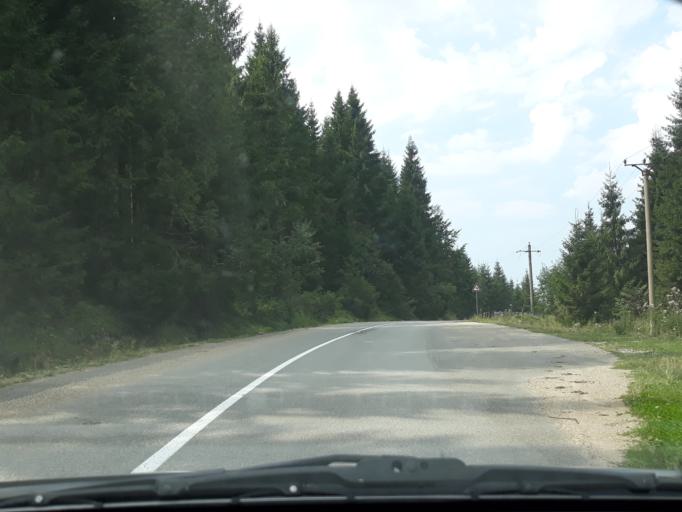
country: RO
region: Bihor
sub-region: Comuna Pietroasa
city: Pietroasa
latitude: 46.5926
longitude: 22.6822
